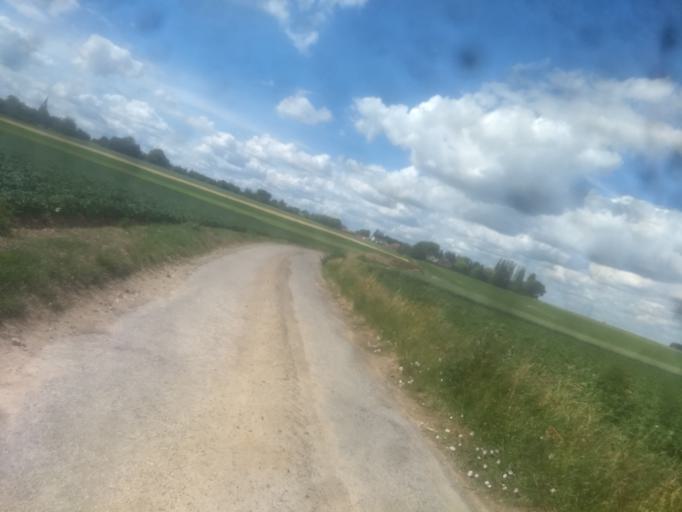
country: FR
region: Nord-Pas-de-Calais
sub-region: Departement du Pas-de-Calais
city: Tilloy-les-Mofflaines
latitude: 50.2430
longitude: 2.8295
